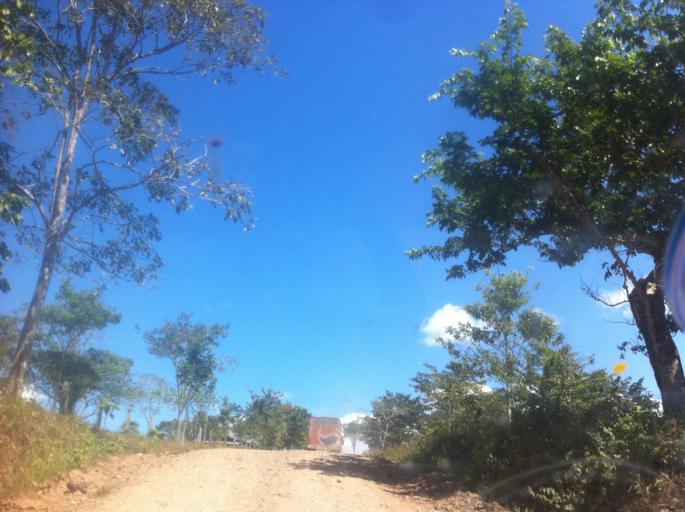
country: CR
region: Alajuela
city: Los Chiles
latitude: 11.2492
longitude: -84.4559
